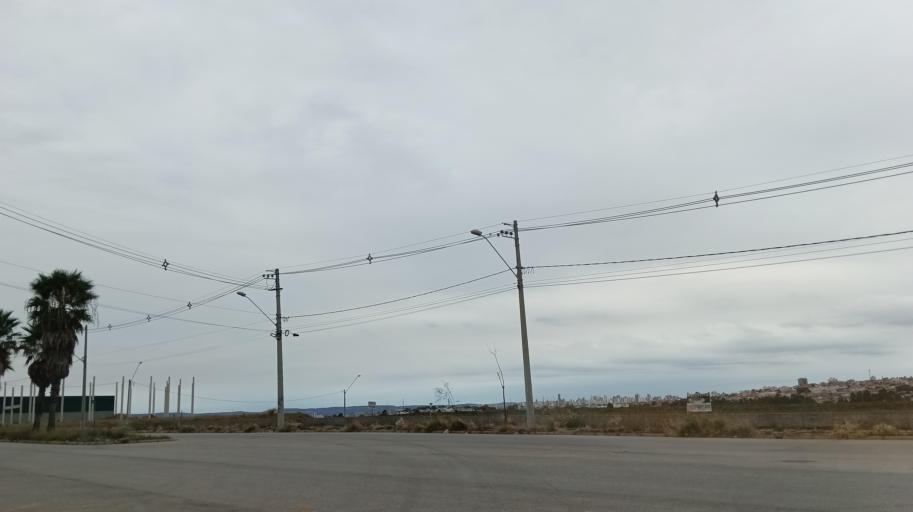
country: BR
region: Sao Paulo
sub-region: Sorocaba
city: Sorocaba
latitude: -23.4585
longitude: -47.4548
